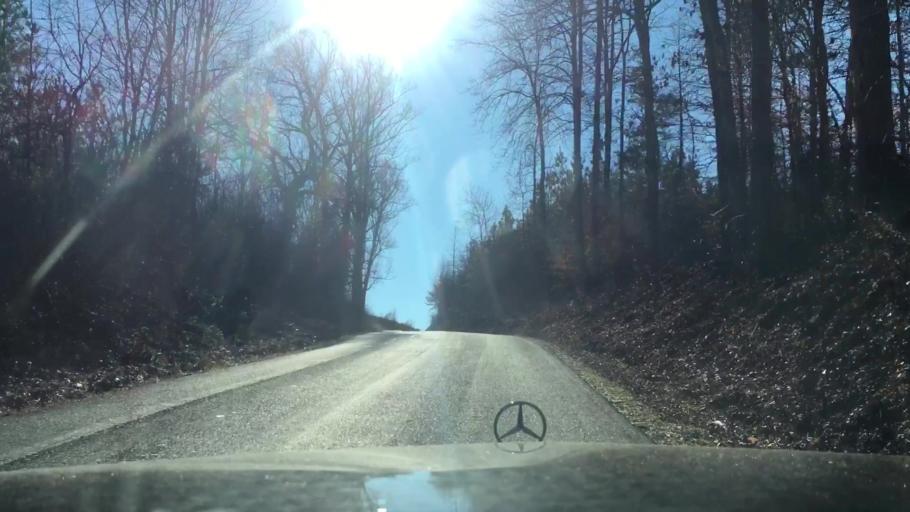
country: US
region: Virginia
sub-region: Campbell County
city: Altavista
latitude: 37.2024
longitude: -79.3089
